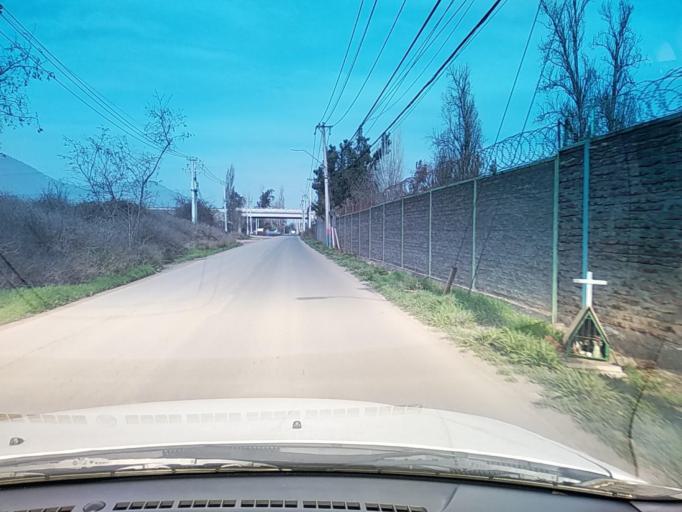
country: CL
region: Santiago Metropolitan
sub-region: Provincia de Chacabuco
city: Chicureo Abajo
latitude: -33.2950
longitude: -70.7240
